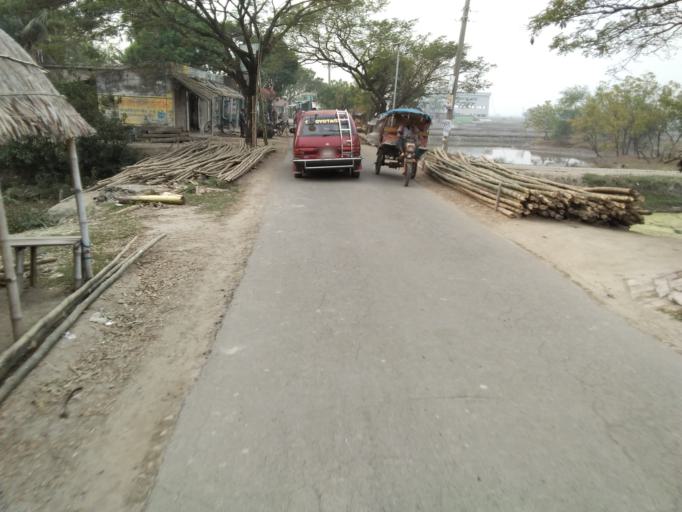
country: BD
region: Khulna
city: Satkhira
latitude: 22.5869
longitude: 89.0652
